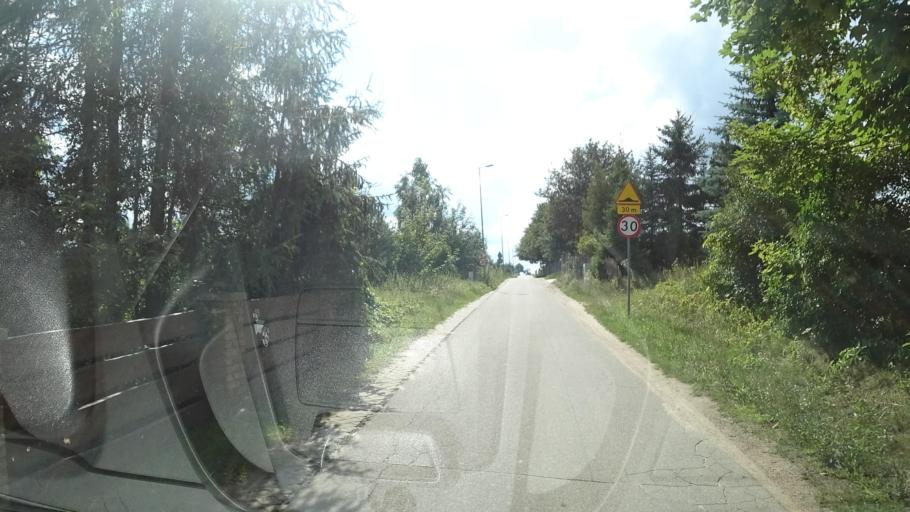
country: PL
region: Podlasie
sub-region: Powiat lomzynski
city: Piatnica
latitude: 53.1398
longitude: 22.1224
